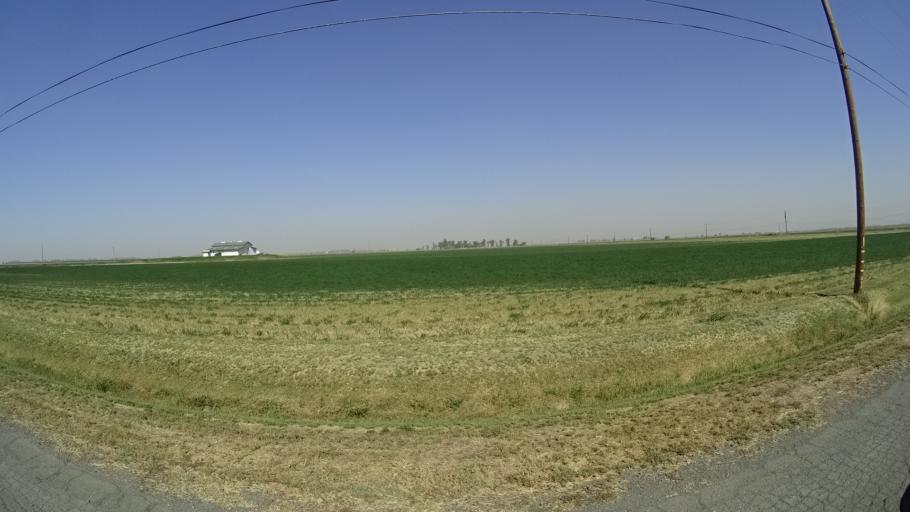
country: US
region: California
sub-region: Yolo County
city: Davis
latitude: 38.5749
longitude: -121.6773
